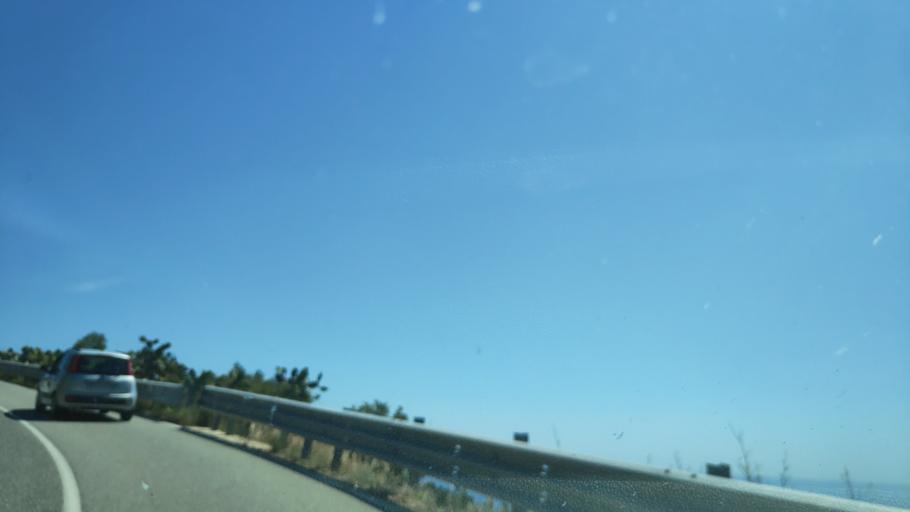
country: IT
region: Calabria
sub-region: Provincia di Catanzaro
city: Montauro
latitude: 38.7461
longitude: 16.5185
